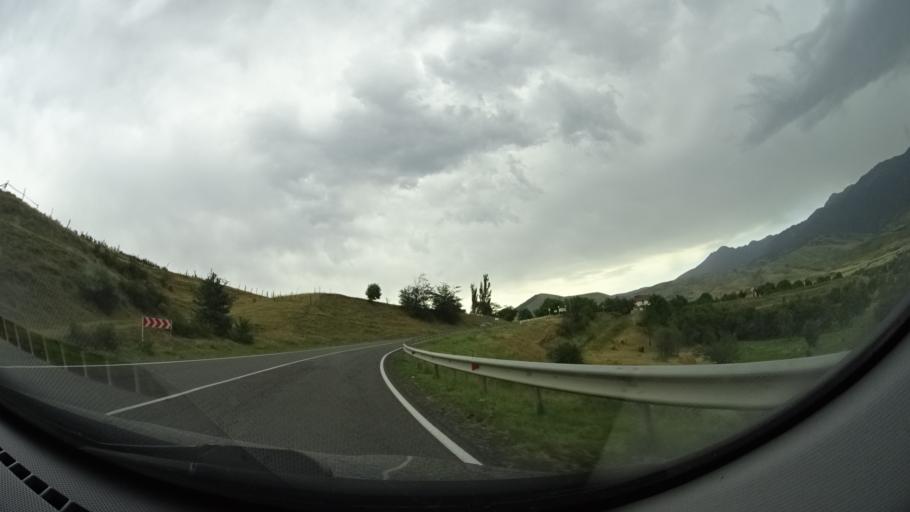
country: GE
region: Samtskhe-Javakheti
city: Aspindza
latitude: 41.7173
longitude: 43.1442
